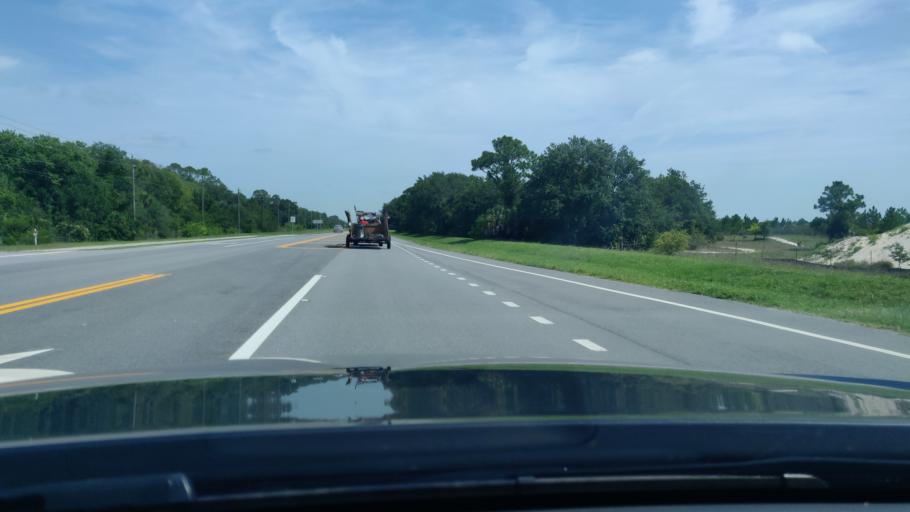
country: US
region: Florida
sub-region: Flagler County
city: Flagler Beach
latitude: 29.5018
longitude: -81.1586
